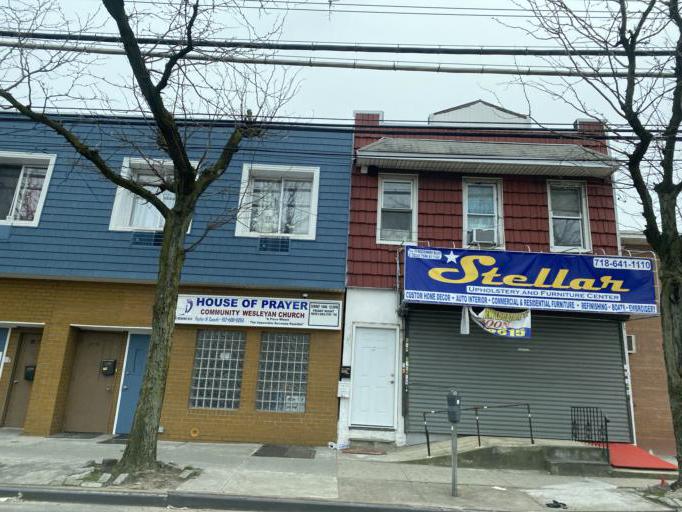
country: US
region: New York
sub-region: Queens County
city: Borough of Queens
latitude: 40.6767
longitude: -73.8232
